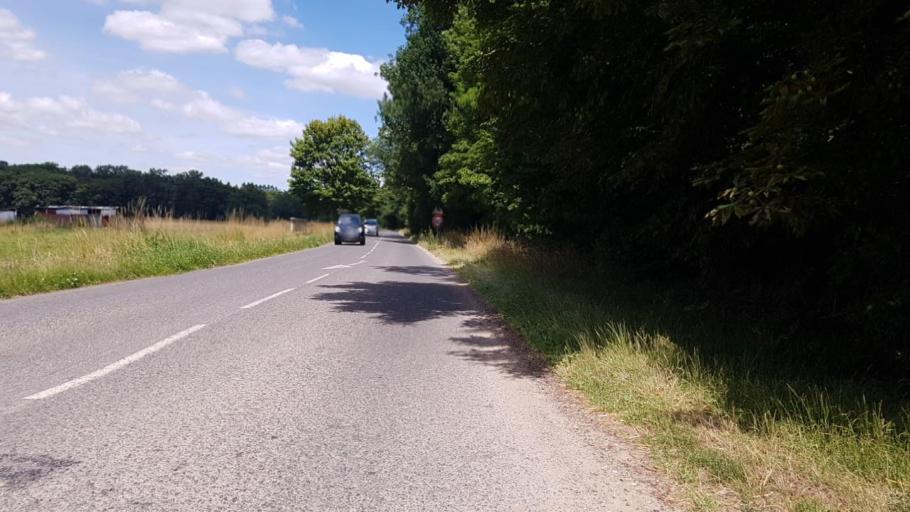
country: FR
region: Picardie
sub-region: Departement de l'Oise
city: Tracy-le-Mont
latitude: 49.5045
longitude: 2.9809
